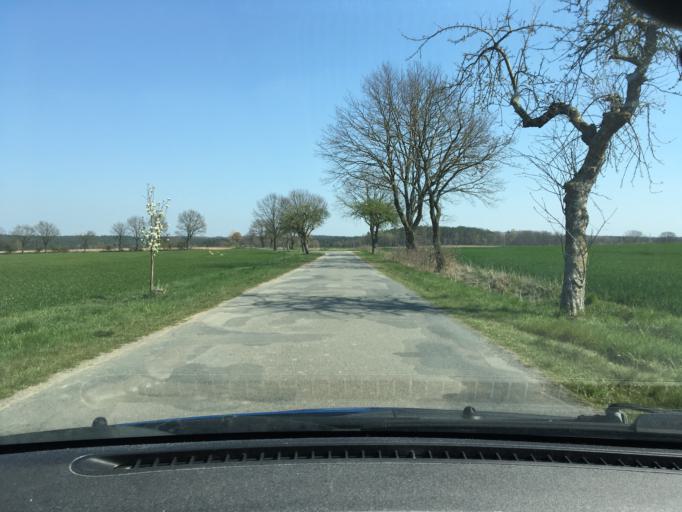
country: DE
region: Lower Saxony
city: Reinstorf
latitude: 53.2006
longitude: 10.5891
